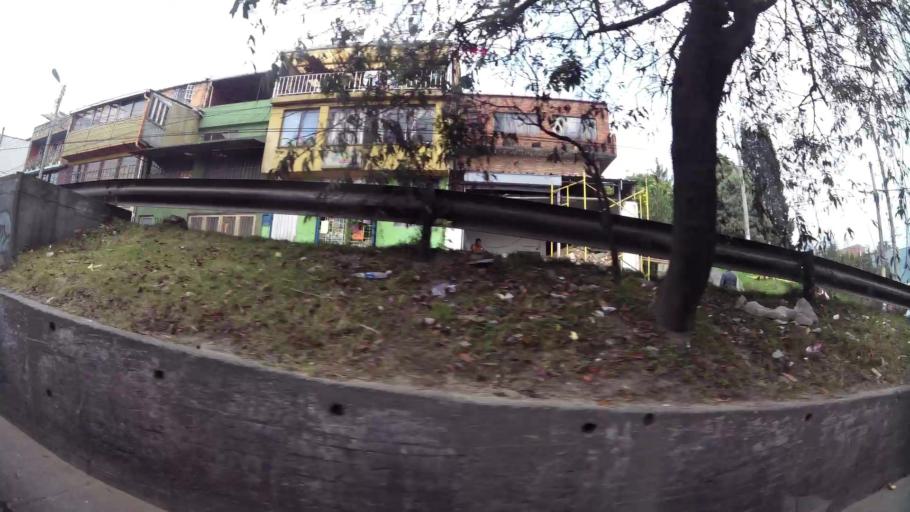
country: CO
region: Bogota D.C.
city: Bogota
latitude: 4.5641
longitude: -74.1080
